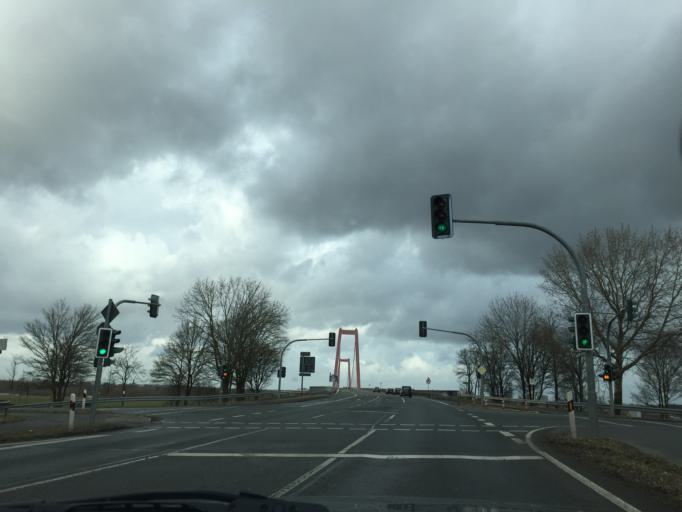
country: DE
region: North Rhine-Westphalia
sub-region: Regierungsbezirk Dusseldorf
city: Emmerich
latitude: 51.8210
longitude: 6.2256
